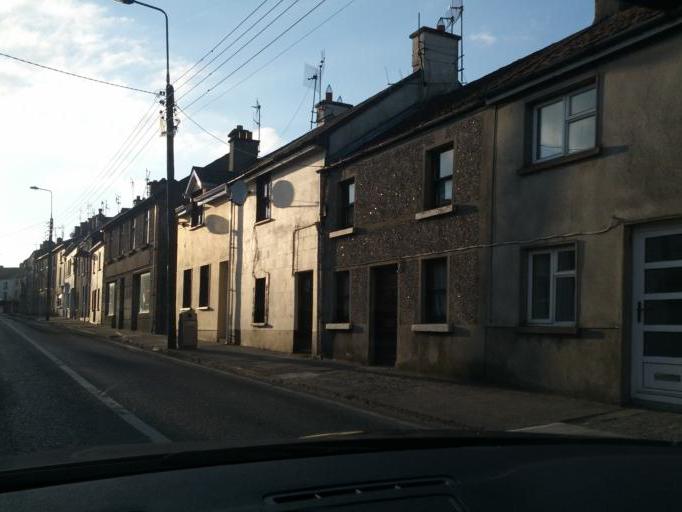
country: IE
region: Munster
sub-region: North Tipperary
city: Nenagh
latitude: 52.8646
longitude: -8.1948
